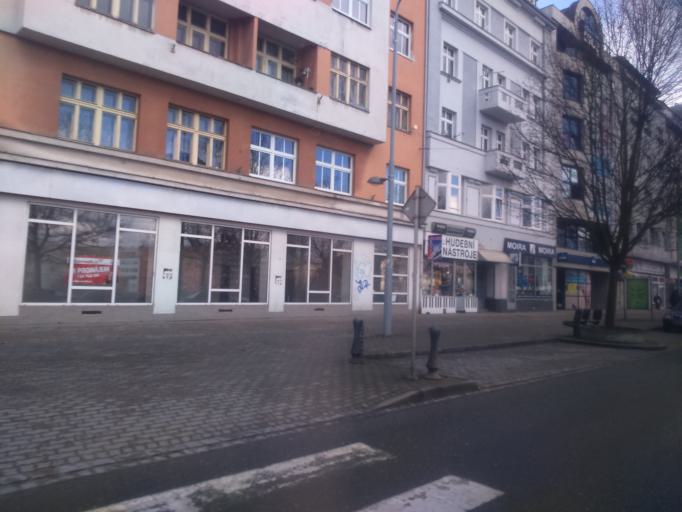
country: CZ
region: Plzensky
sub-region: Okres Plzen-Mesto
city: Pilsen
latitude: 49.7433
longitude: 13.3828
